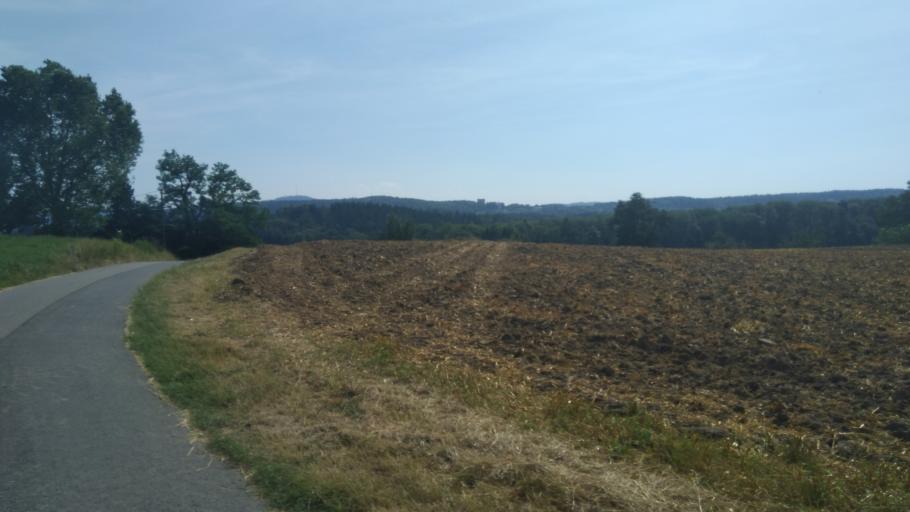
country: CH
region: Zurich
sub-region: Bezirk Zuerich
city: Zuerich (Kreis 11) / Seebach
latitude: 47.4321
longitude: 8.5373
